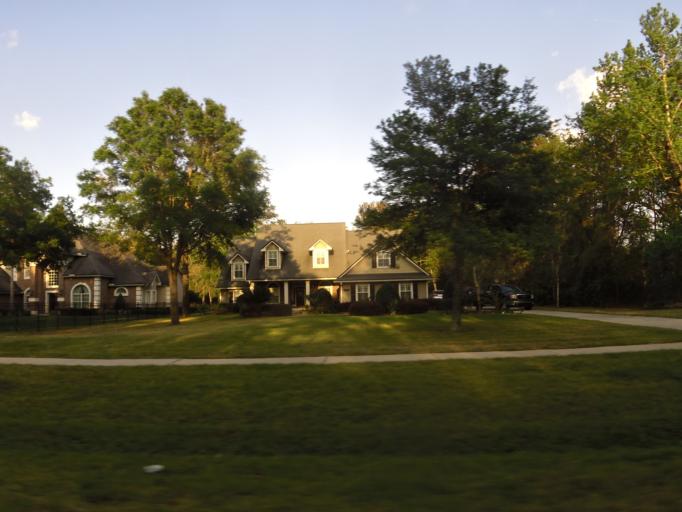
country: US
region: Florida
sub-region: Saint Johns County
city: Fruit Cove
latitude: 30.1177
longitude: -81.5759
